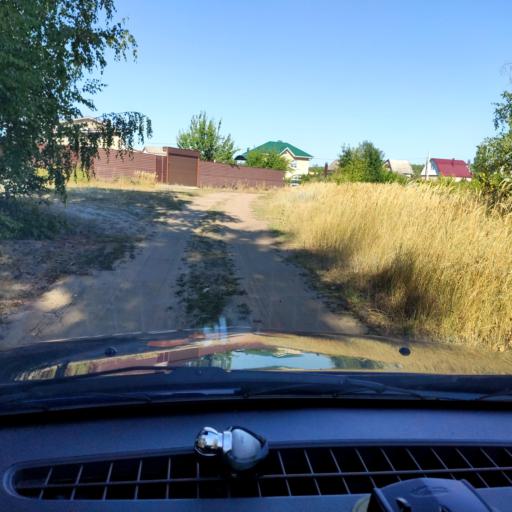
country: RU
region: Voronezj
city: Maslovka
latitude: 51.5439
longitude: 39.1710
